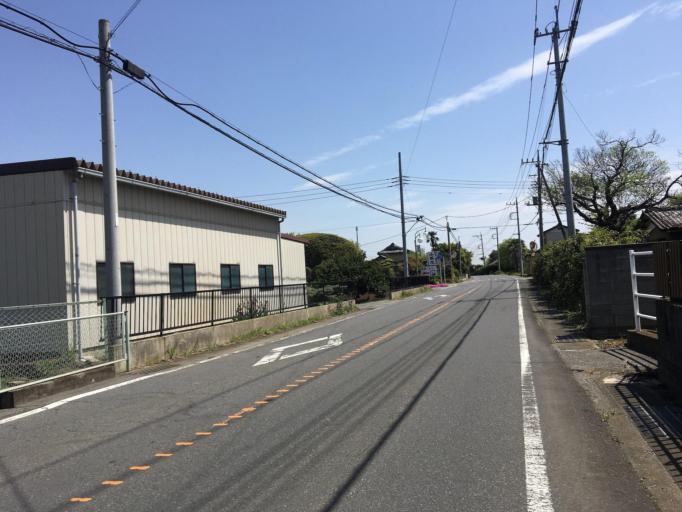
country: JP
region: Gunma
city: Sakai-nakajima
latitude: 36.2799
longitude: 139.2902
